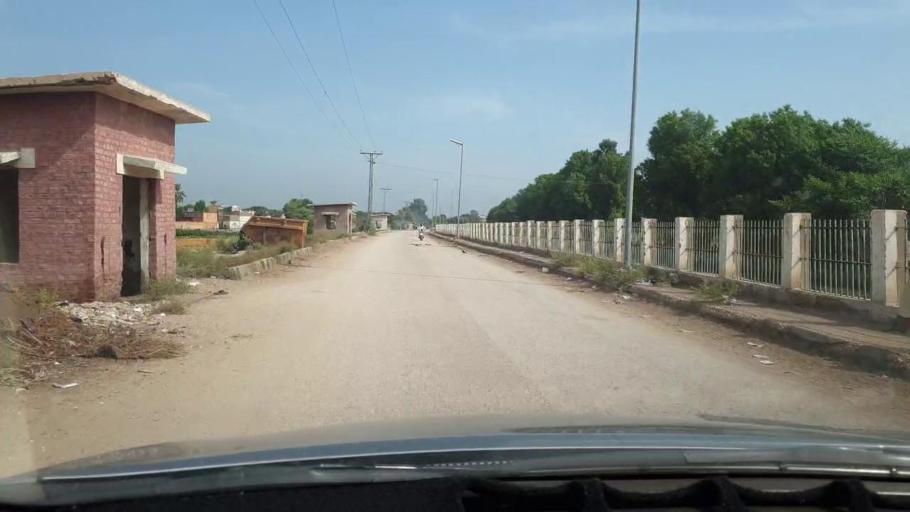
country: PK
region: Sindh
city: Khairpur
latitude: 27.5268
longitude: 68.7540
